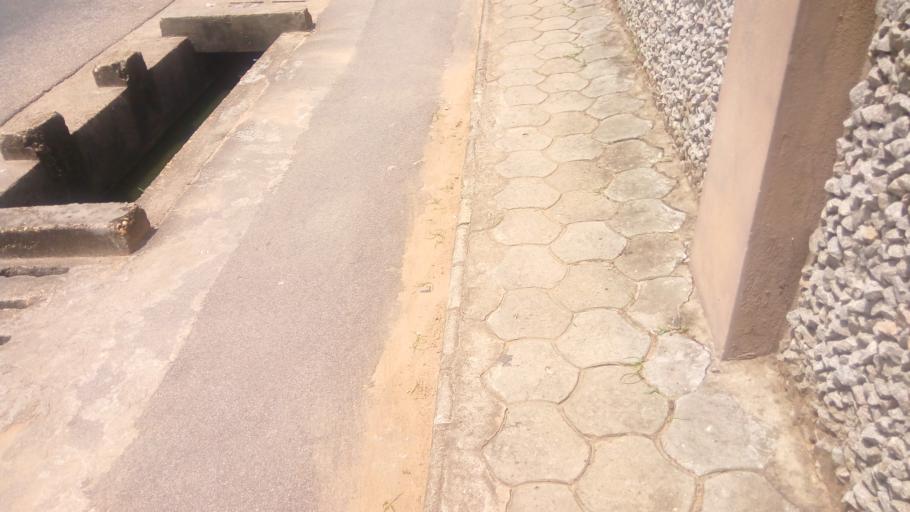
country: CI
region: Lagunes
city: Abidjan
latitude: 5.3361
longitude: -4.0234
